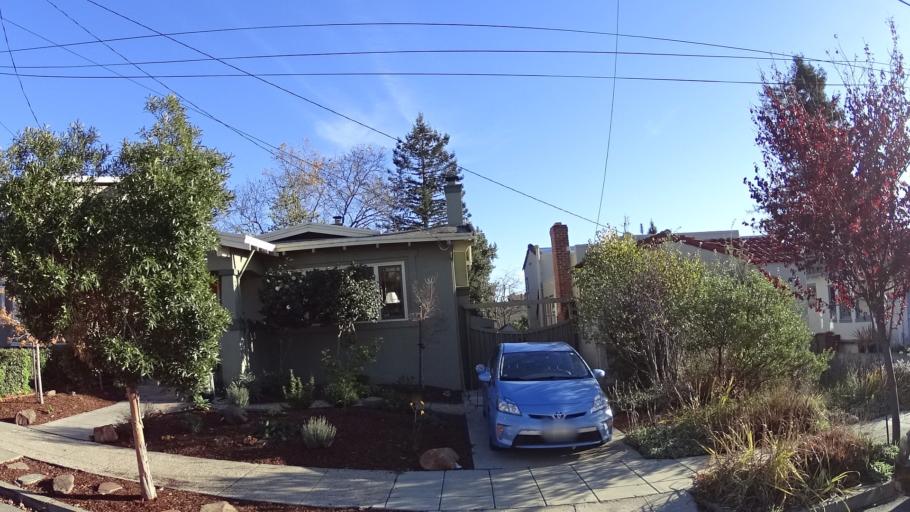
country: US
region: California
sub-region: Alameda County
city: Piedmont
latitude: 37.8088
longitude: -122.2212
